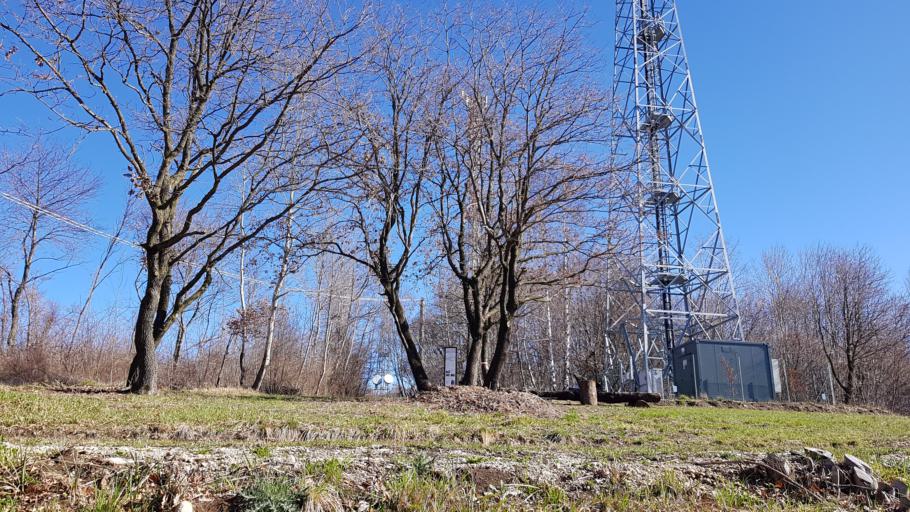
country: IT
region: Friuli Venezia Giulia
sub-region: Provincia di Udine
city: San Pietro al Natisone
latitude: 46.1046
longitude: 13.4863
